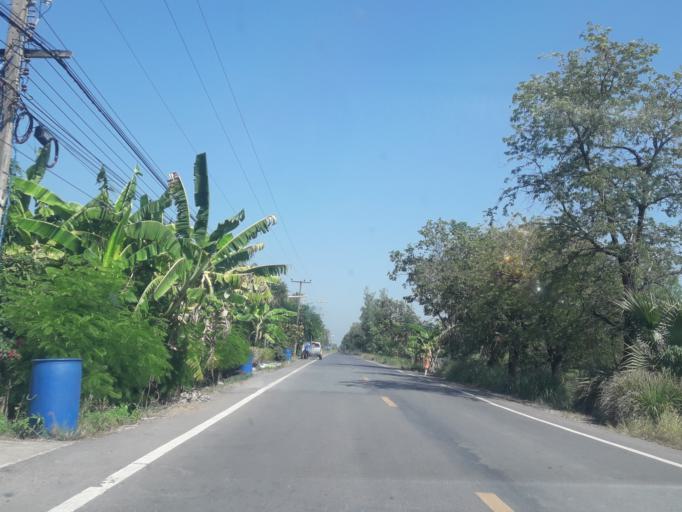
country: TH
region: Pathum Thani
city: Nong Suea
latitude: 14.1530
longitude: 100.8459
